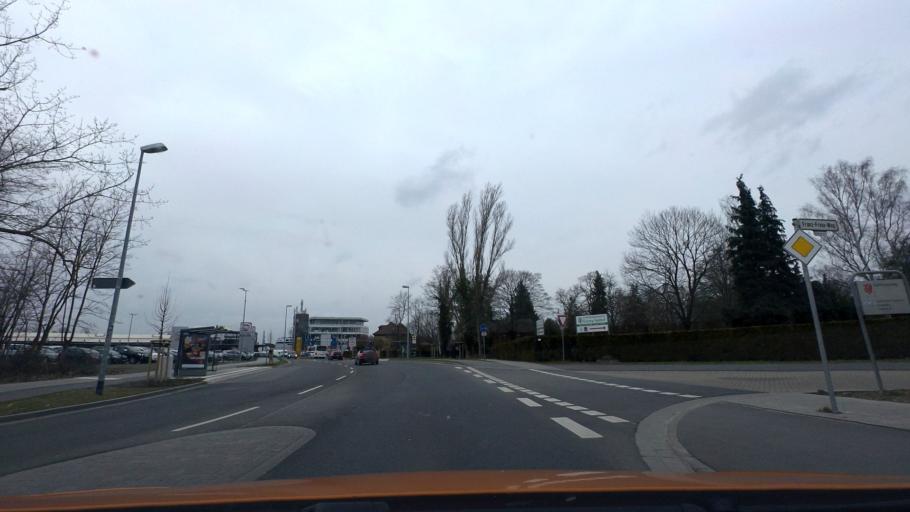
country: DE
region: Lower Saxony
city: Braunschweig
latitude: 52.2532
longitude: 10.5698
